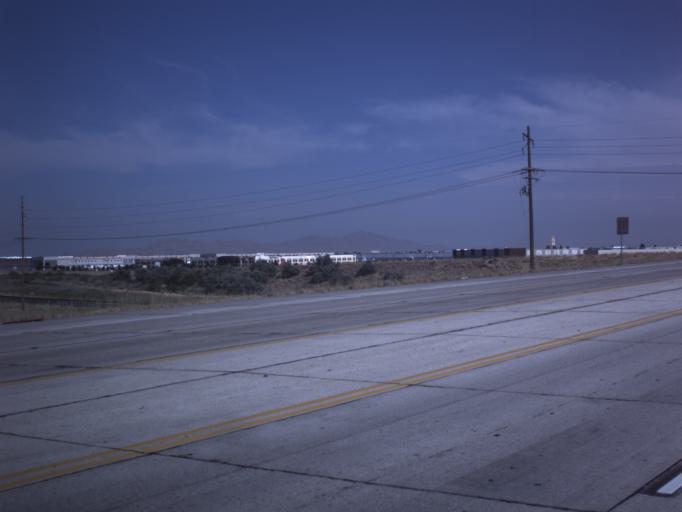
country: US
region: Utah
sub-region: Salt Lake County
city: West Valley City
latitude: 40.7675
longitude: -112.0249
